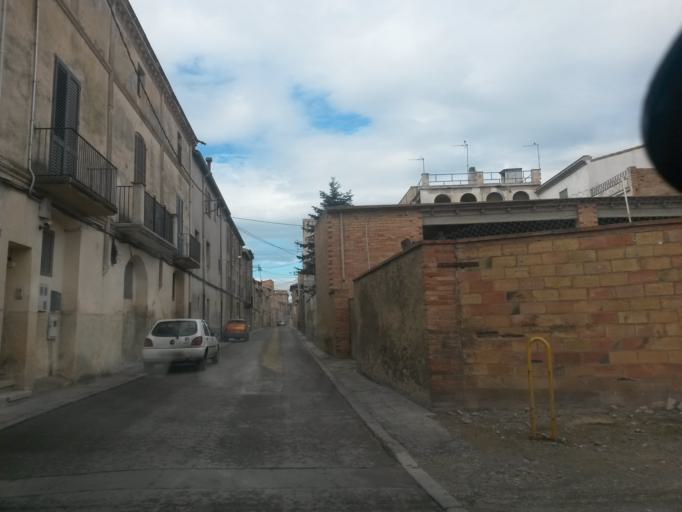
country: ES
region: Catalonia
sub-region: Provincia de Girona
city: Cabanes
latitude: 42.3094
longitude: 2.9750
